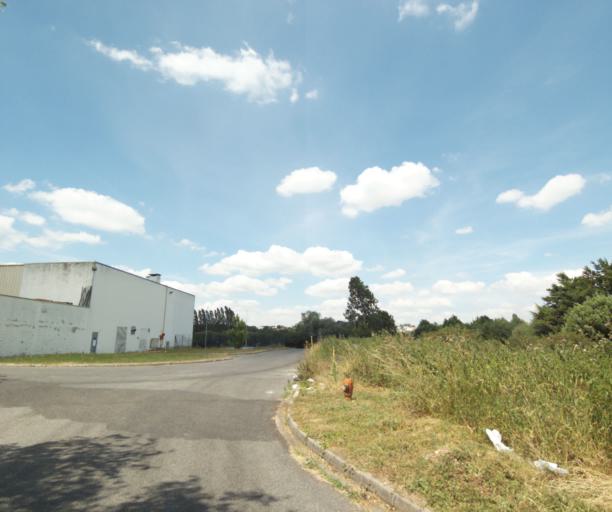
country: FR
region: Lorraine
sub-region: Departement de Meurthe-et-Moselle
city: Luneville
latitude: 48.5990
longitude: 6.4968
